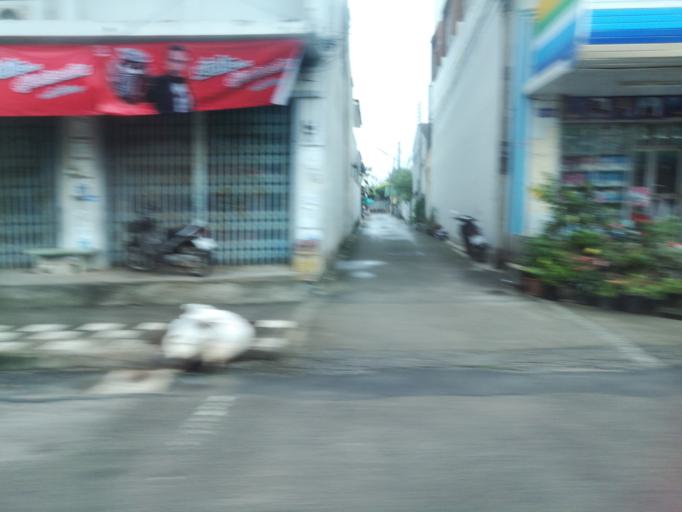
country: TH
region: Prachuap Khiri Khan
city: Prachuap Khiri Khan
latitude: 11.8039
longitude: 99.7962
